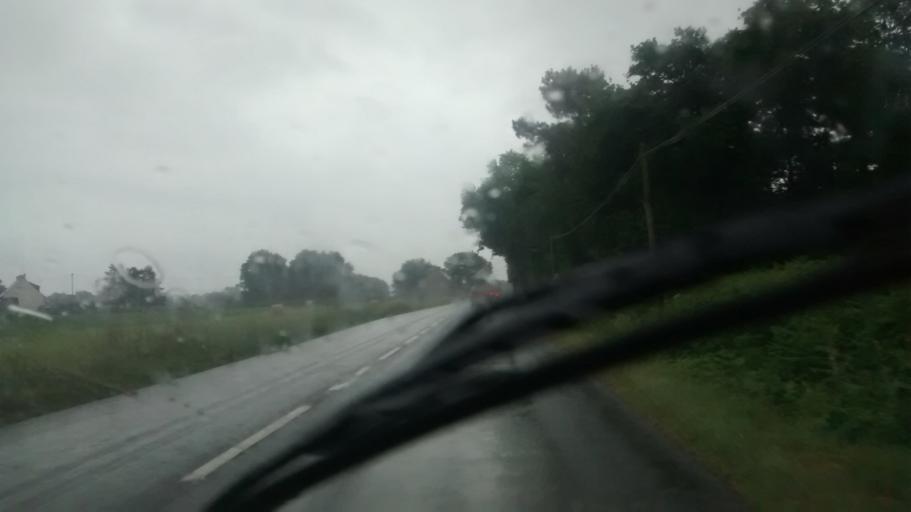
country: FR
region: Brittany
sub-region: Departement du Morbihan
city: La Gacilly
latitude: 47.7777
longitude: -2.1607
